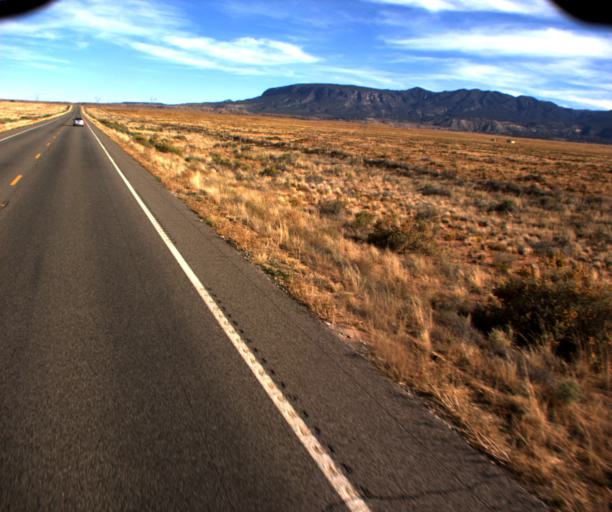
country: US
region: Arizona
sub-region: Apache County
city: Lukachukai
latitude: 36.9420
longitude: -109.2557
